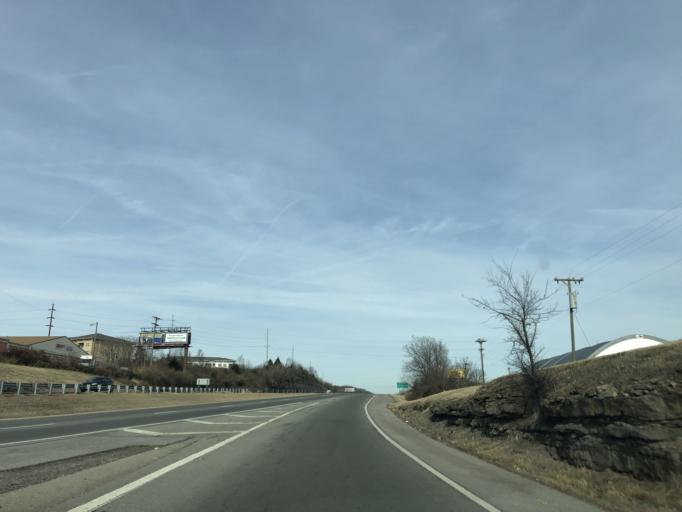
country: US
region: Tennessee
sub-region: Davidson County
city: Nashville
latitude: 36.2058
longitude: -86.7497
